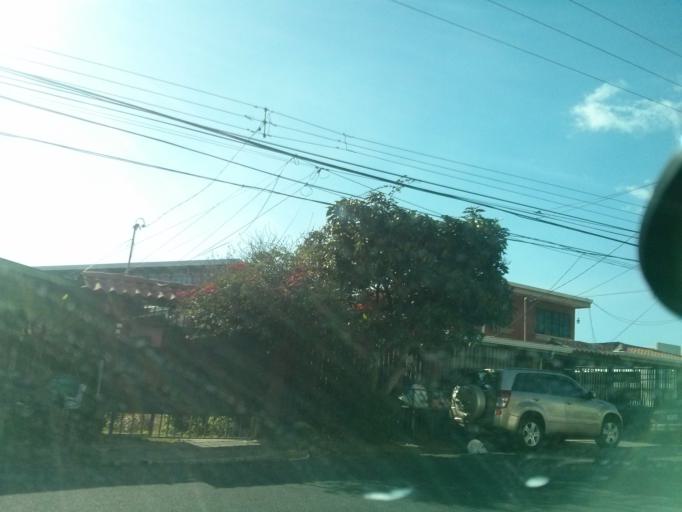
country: CR
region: San Jose
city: Sabanilla
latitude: 9.9376
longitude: -84.0410
